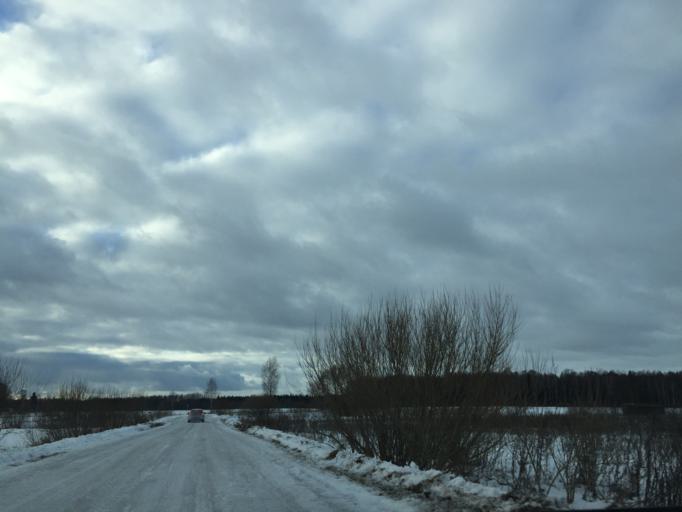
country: LV
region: Lielvarde
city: Lielvarde
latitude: 56.6280
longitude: 24.7434
